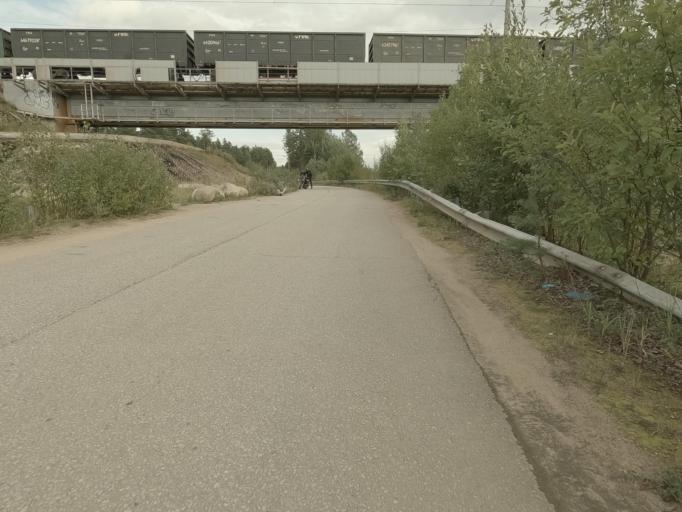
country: RU
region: Leningrad
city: Mga
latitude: 59.7604
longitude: 31.0178
